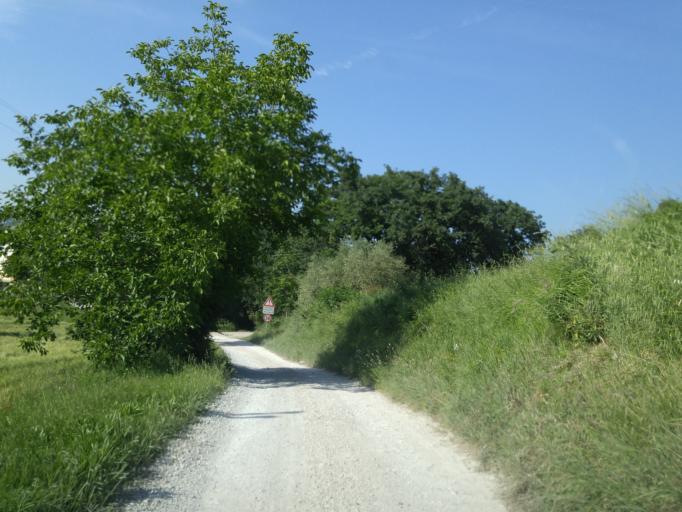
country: IT
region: The Marches
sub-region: Provincia di Pesaro e Urbino
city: Tavernelle
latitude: 43.7243
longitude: 12.9002
